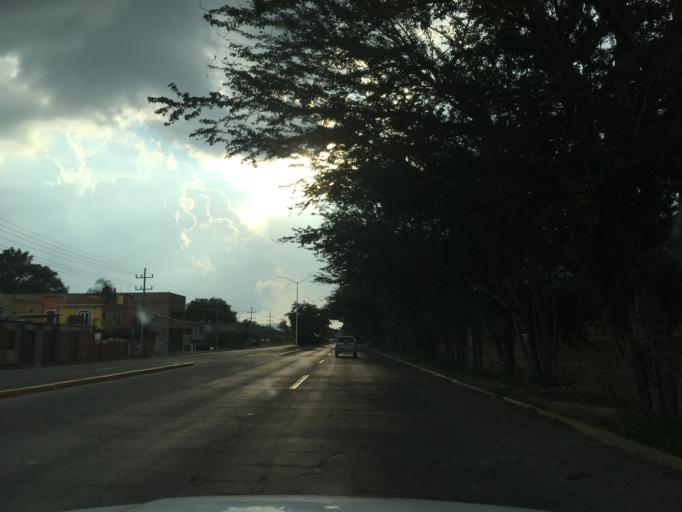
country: MX
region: Jalisco
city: Tlajomulco de Zuniga
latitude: 20.4882
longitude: -103.4603
